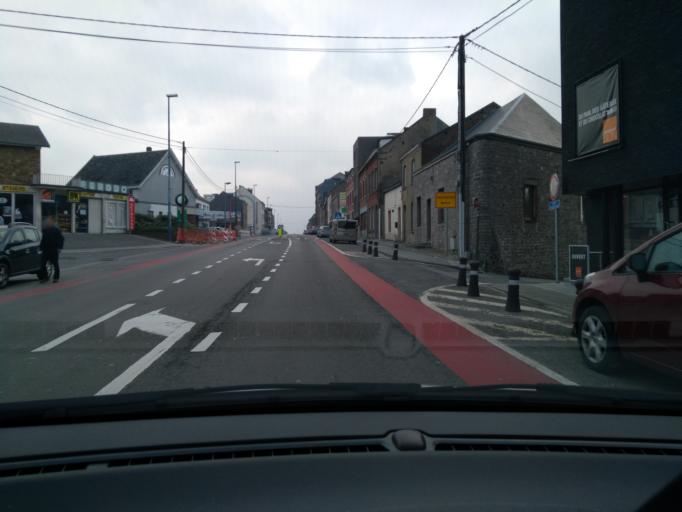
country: BE
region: Wallonia
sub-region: Province de Namur
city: Namur
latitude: 50.4723
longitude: 4.8295
